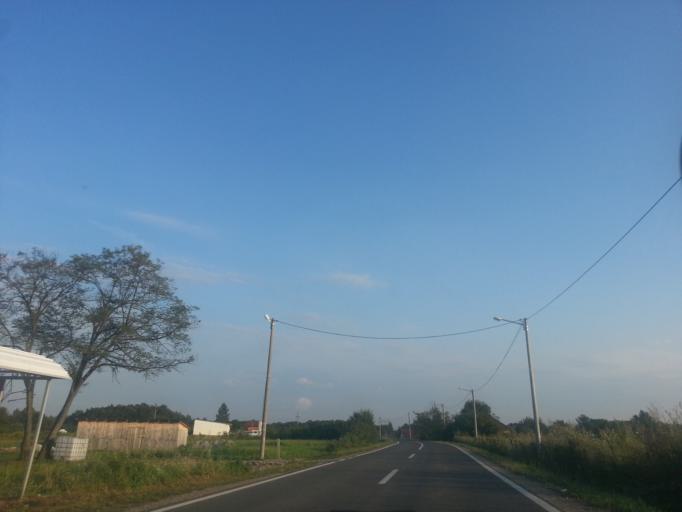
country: BA
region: Brcko
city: Brcko
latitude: 44.8115
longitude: 18.8091
